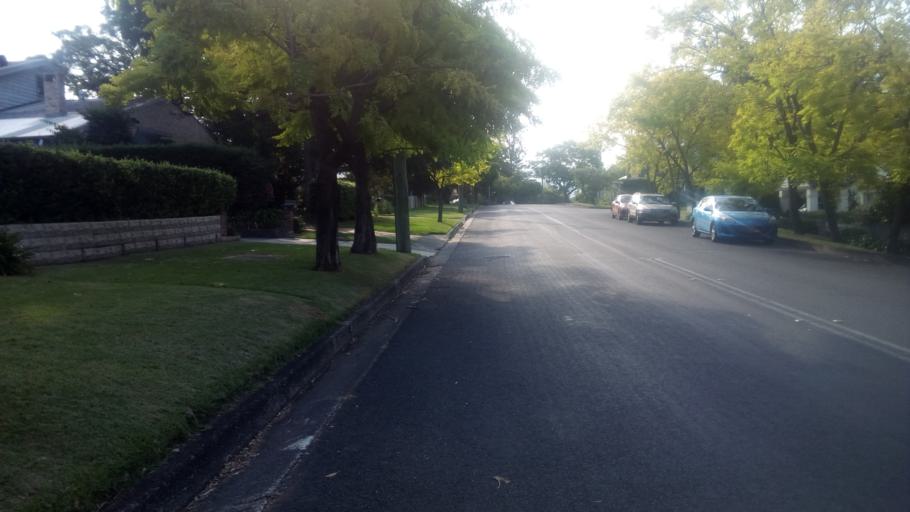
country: AU
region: New South Wales
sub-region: Wollongong
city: Mangerton
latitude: -34.4313
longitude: 150.8757
